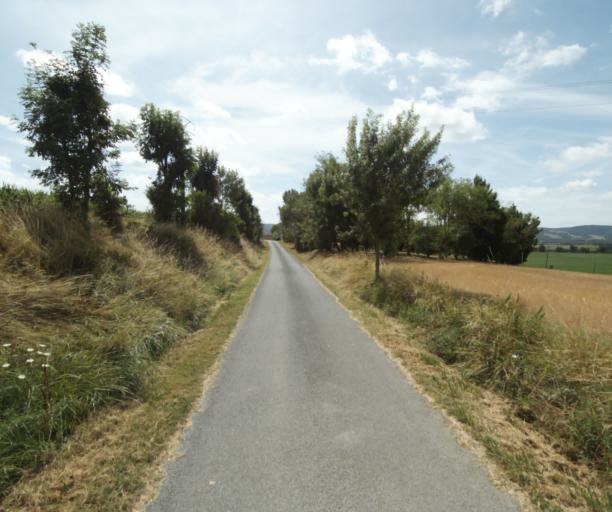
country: FR
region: Midi-Pyrenees
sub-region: Departement du Tarn
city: Dourgne
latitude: 43.5016
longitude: 2.0947
